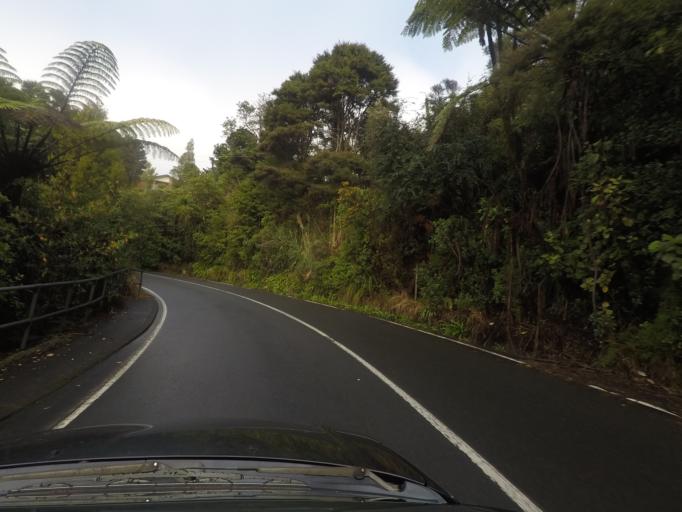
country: NZ
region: Auckland
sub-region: Auckland
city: Titirangi
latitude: -36.9233
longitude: 174.5834
